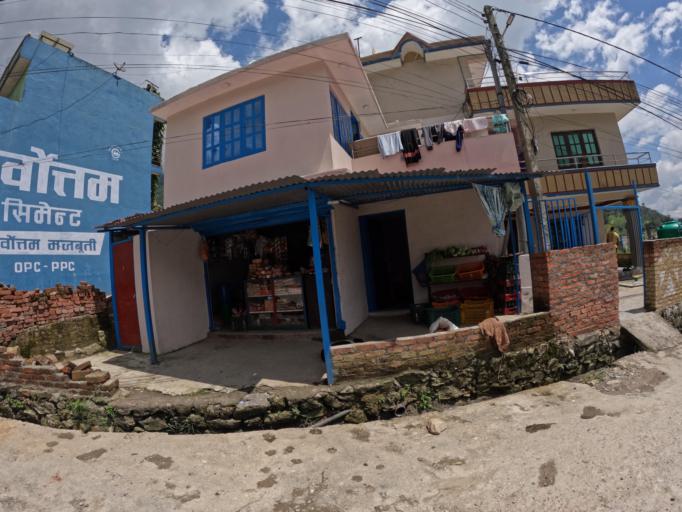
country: NP
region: Central Region
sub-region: Bagmati Zone
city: Kathmandu
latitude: 27.7956
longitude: 85.3305
